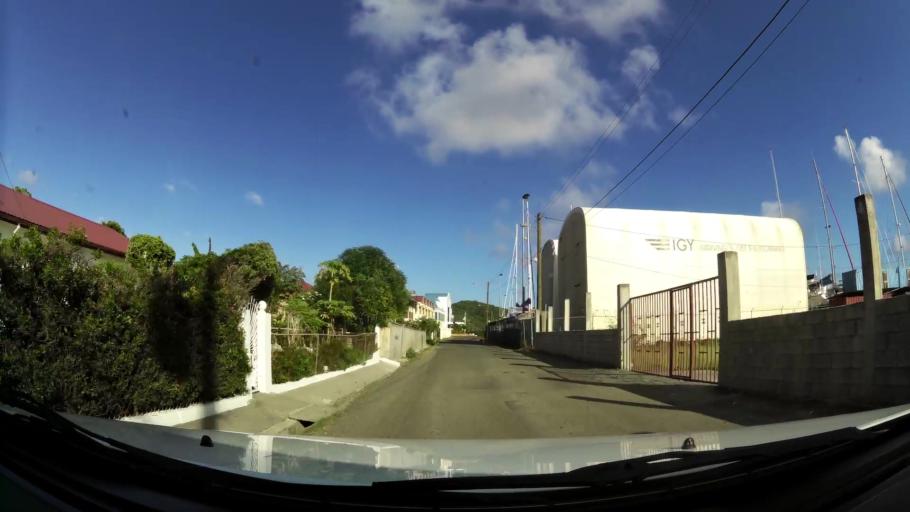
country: LC
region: Gros-Islet
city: Gros Islet
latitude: 14.0789
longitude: -60.9502
